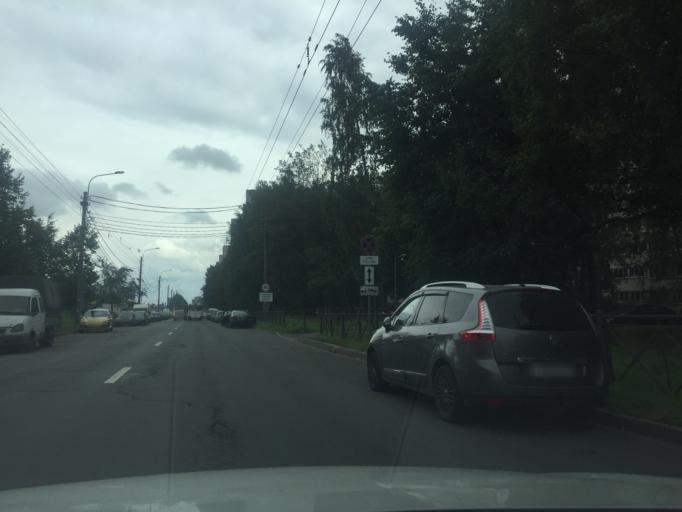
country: RU
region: Leningrad
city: Parnas
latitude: 60.0570
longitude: 30.3535
